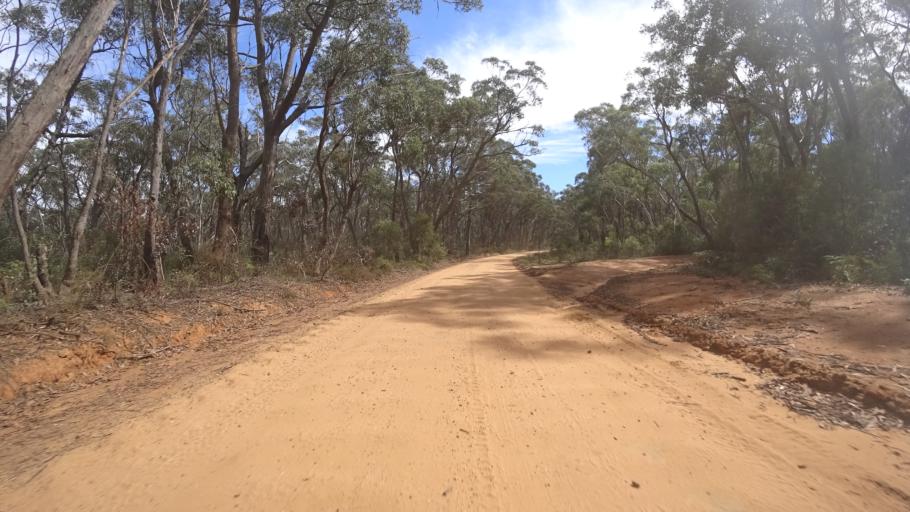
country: AU
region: New South Wales
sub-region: Lithgow
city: Lithgow
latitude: -33.3147
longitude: 150.2398
